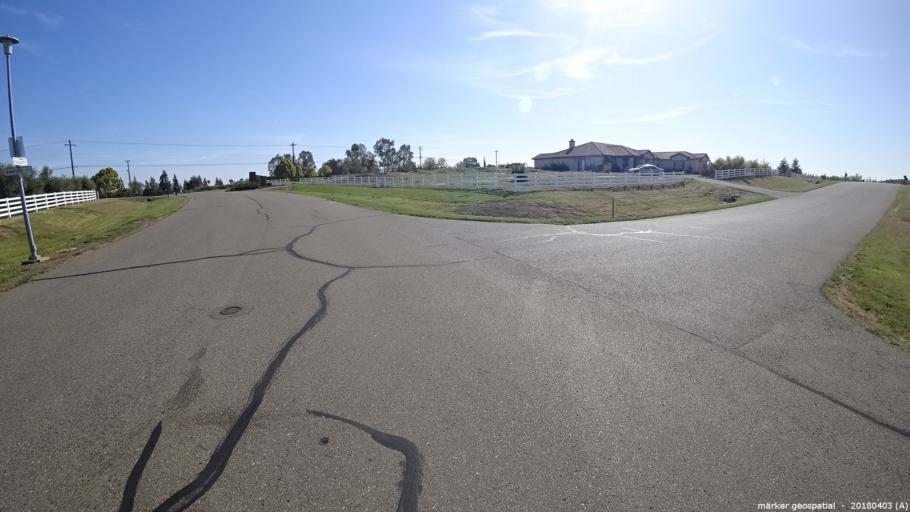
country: US
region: California
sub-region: Sacramento County
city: Wilton
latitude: 38.4232
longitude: -121.1945
